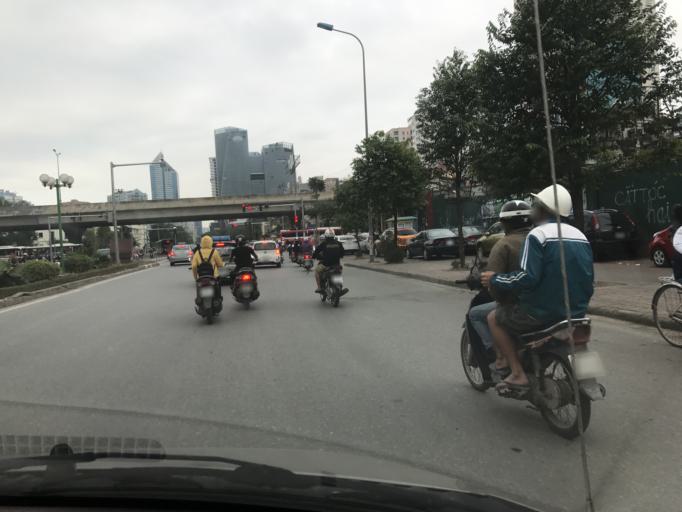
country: VN
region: Ha Noi
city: Thanh Xuan
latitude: 20.9987
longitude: 105.7961
